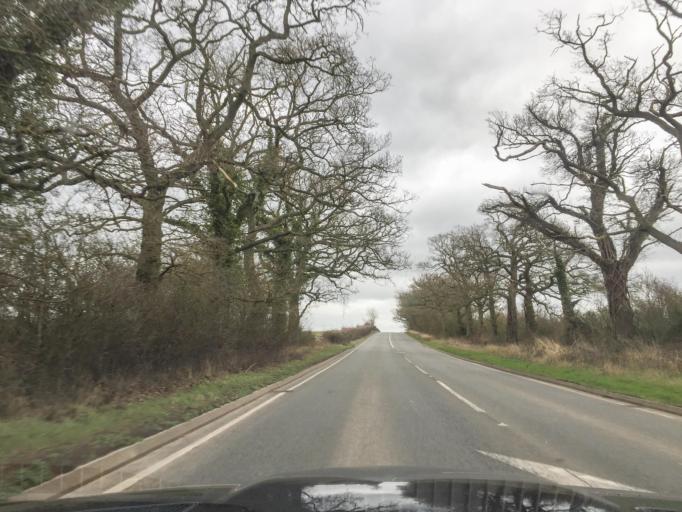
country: GB
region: England
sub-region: Warwickshire
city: Wellesbourne Mountford
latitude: 52.1258
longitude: -1.5652
